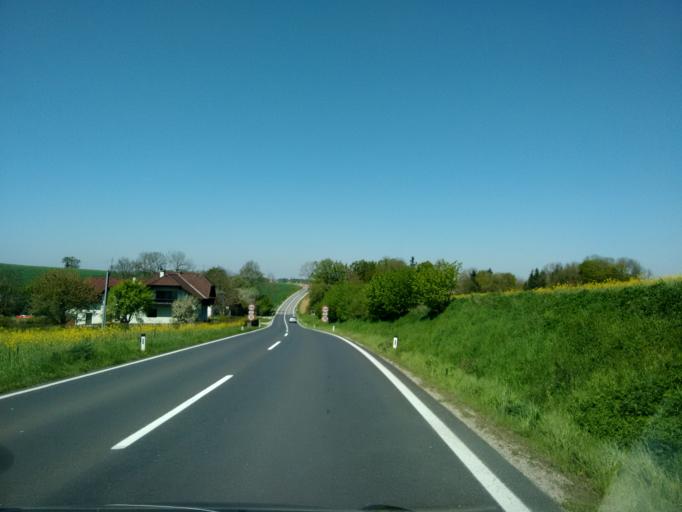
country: AT
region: Upper Austria
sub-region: Politischer Bezirk Kirchdorf an der Krems
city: Kremsmunster
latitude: 48.0660
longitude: 14.0935
